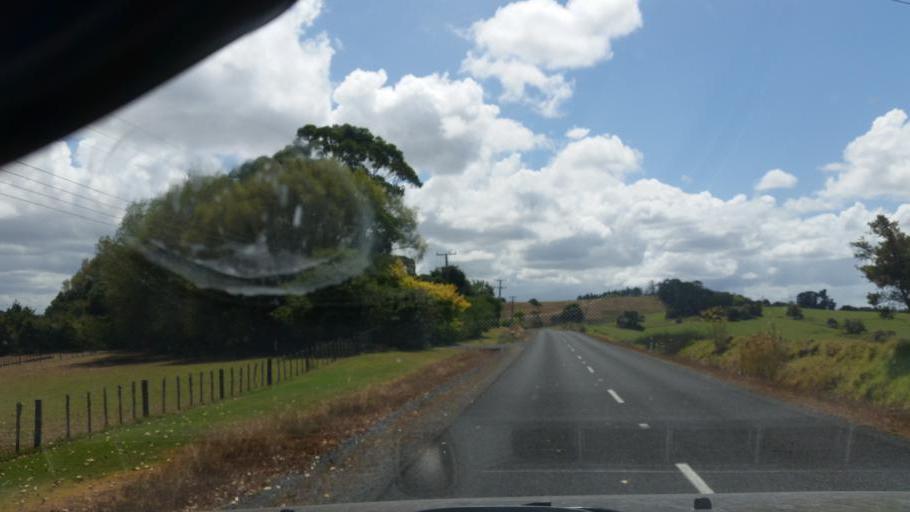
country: NZ
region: Northland
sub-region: Whangarei
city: Ruakaka
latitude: -36.1363
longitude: 174.2264
